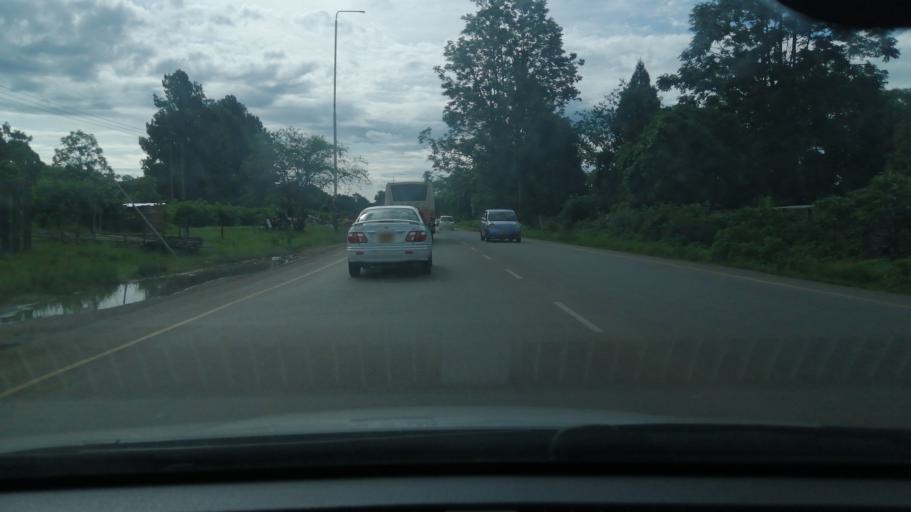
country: ZW
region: Harare
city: Harare
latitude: -17.7647
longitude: 30.9954
